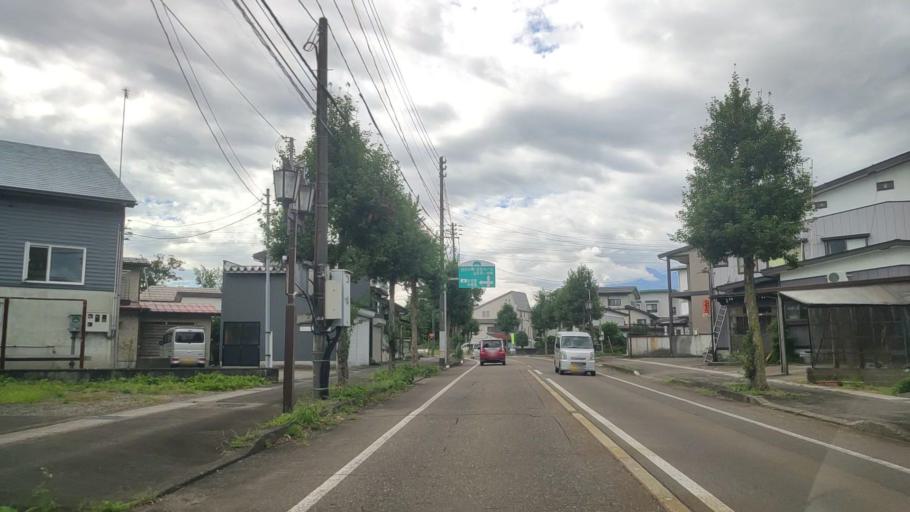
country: JP
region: Niigata
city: Arai
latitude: 37.0267
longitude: 138.2465
